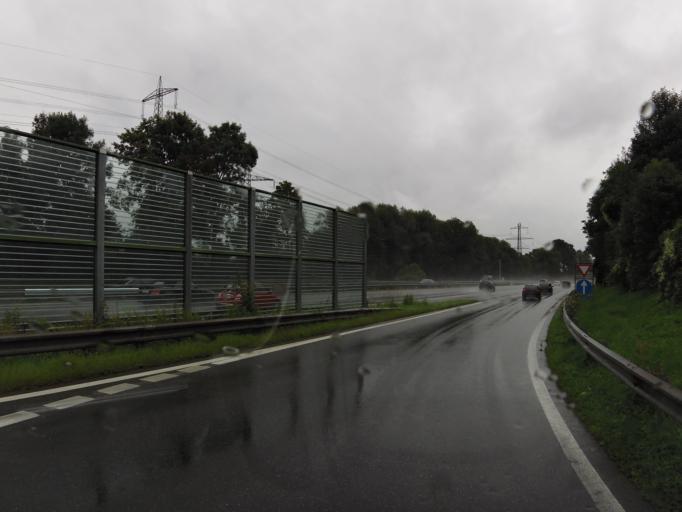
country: AT
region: Vorarlberg
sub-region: Politischer Bezirk Feldkirch
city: Altach
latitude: 47.3543
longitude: 9.6404
